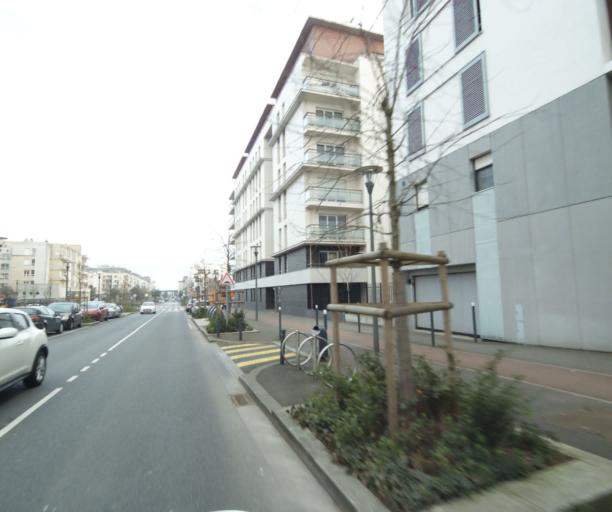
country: FR
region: Ile-de-France
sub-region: Departement du Val-d'Oise
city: Courdimanche
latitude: 49.0512
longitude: 2.0068
